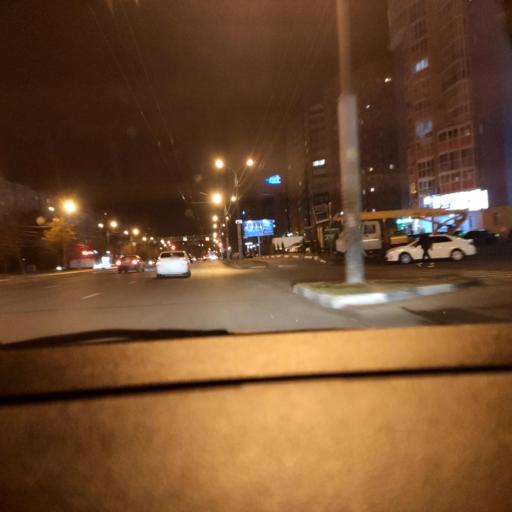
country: RU
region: Voronezj
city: Podgornoye
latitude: 51.7121
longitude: 39.1594
